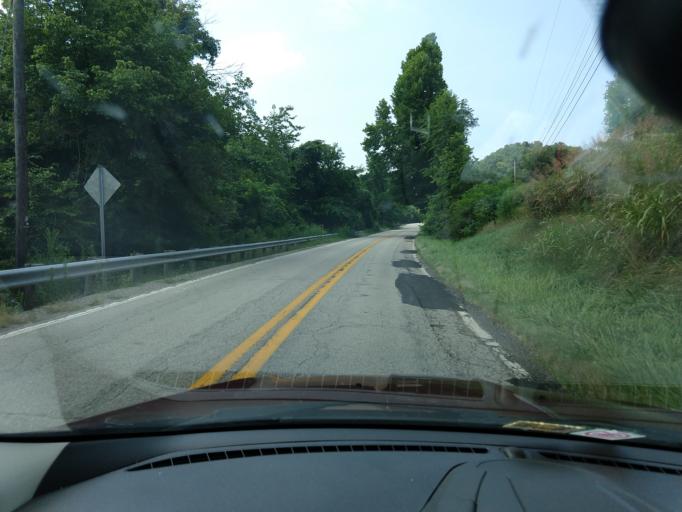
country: US
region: West Virginia
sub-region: Mason County
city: New Haven
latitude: 38.9245
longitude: -81.9128
